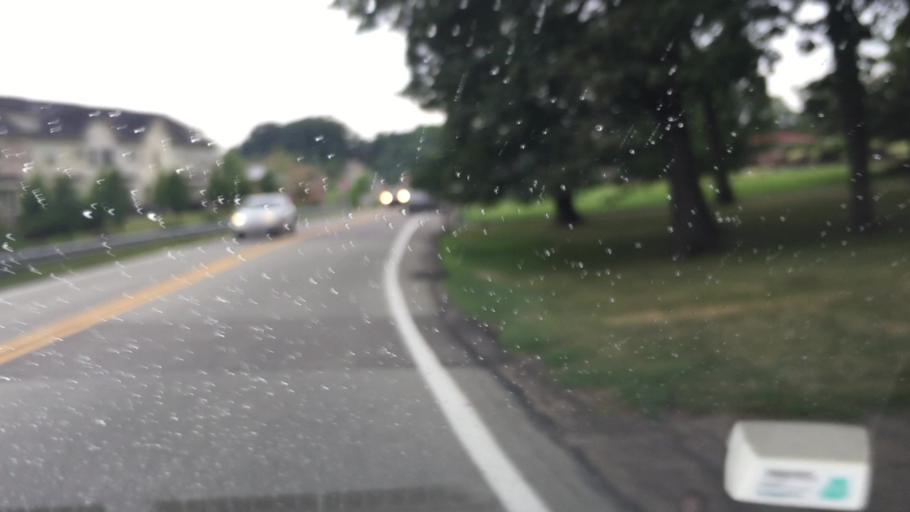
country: US
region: Pennsylvania
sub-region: Allegheny County
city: West View
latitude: 40.5720
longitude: -80.0200
